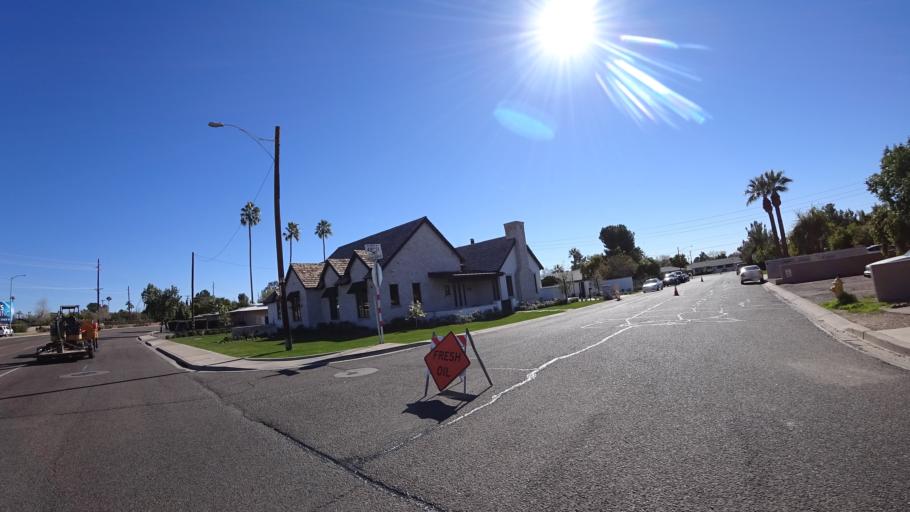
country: US
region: Arizona
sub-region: Maricopa County
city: Paradise Valley
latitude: 33.4945
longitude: -111.9760
